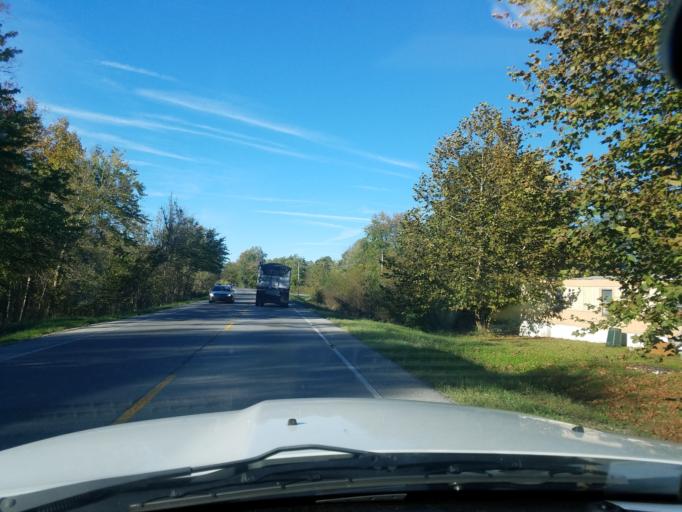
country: US
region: Kentucky
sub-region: Laurel County
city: London
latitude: 37.0733
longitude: -84.0583
